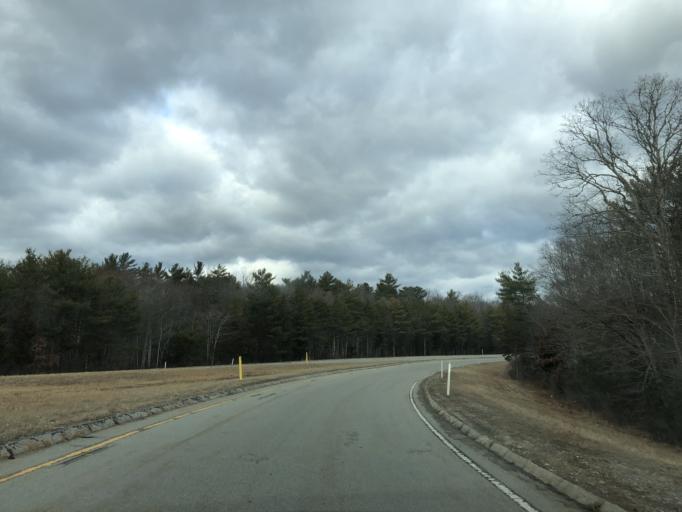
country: US
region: Massachusetts
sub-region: Plymouth County
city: Mattapoisett
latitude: 41.6760
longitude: -70.8233
